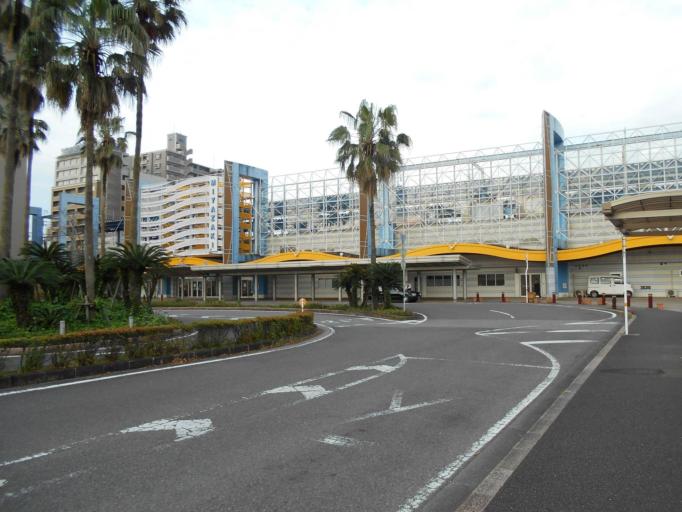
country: JP
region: Miyazaki
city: Miyazaki-shi
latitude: 31.9159
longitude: 131.4326
